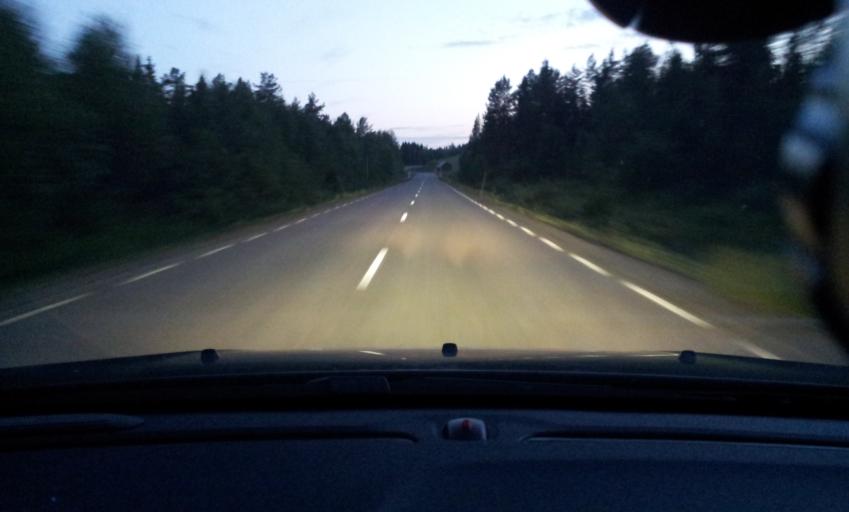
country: SE
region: Jaemtland
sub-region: OEstersunds Kommun
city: Brunflo
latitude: 62.6609
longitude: 14.8685
